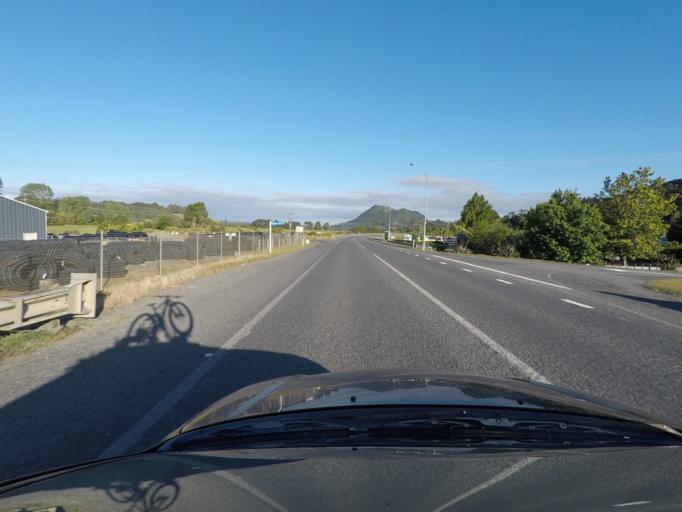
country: NZ
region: Northland
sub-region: Whangarei
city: Whangarei
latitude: -35.6251
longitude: 174.2930
